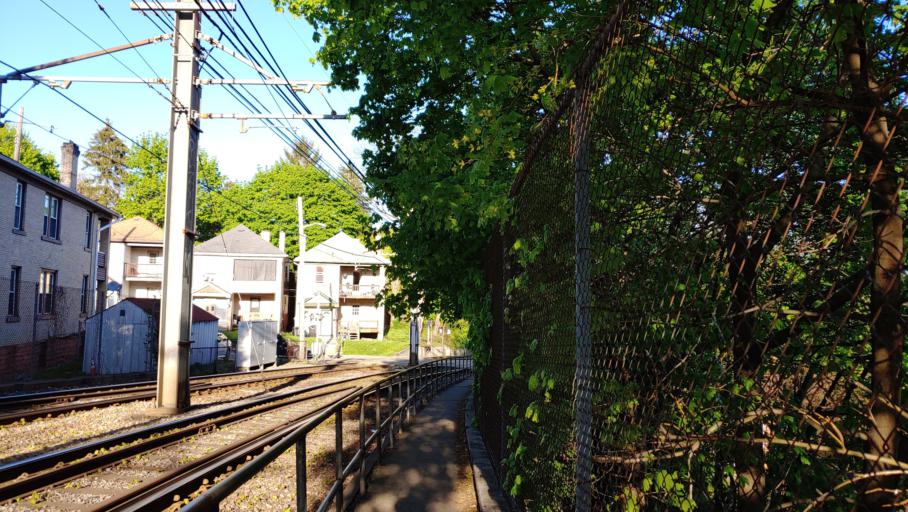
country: US
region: Pennsylvania
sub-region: Allegheny County
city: Dormont
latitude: 40.4111
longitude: -80.0216
